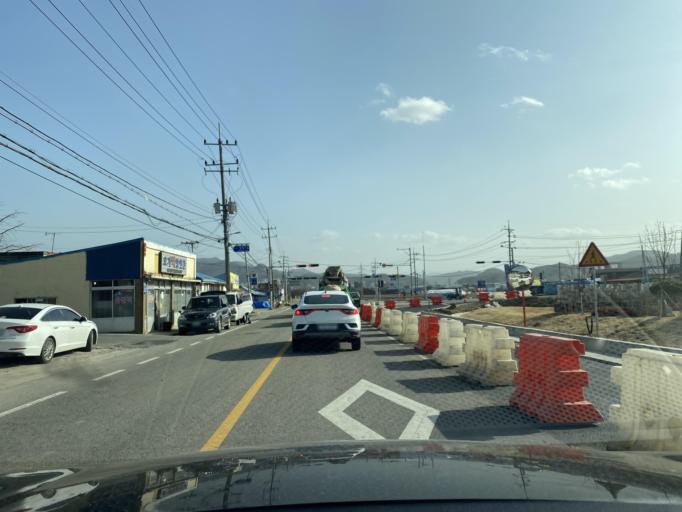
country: KR
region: Chungcheongnam-do
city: Yesan
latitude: 36.6850
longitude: 126.8059
